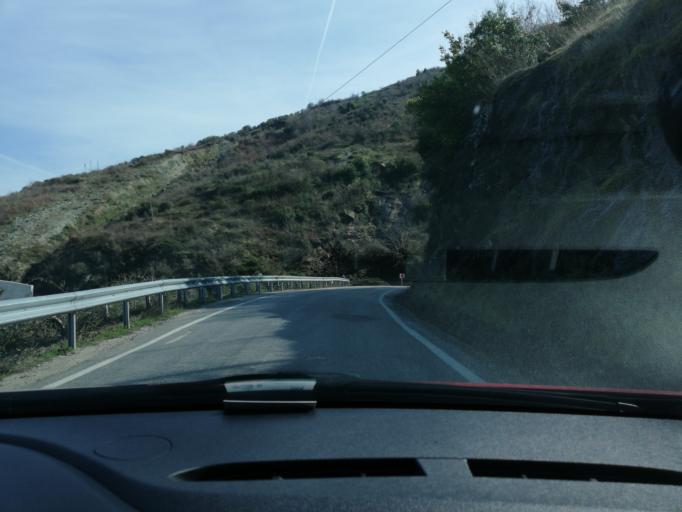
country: TR
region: Bartin
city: Kurucasile
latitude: 41.8270
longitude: 32.6452
